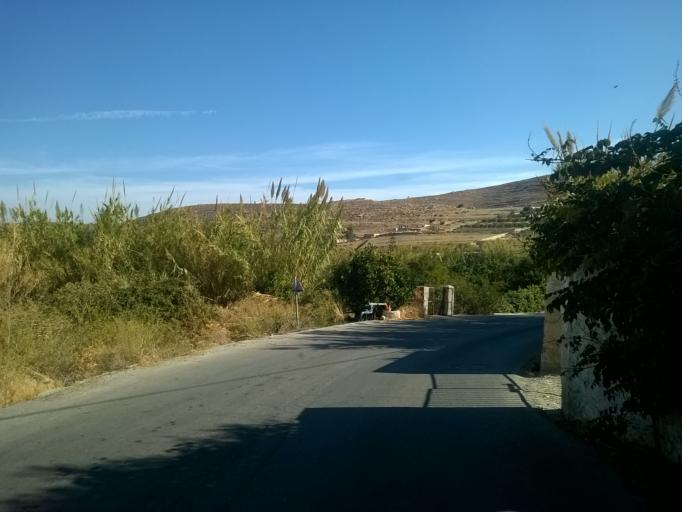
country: GR
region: South Aegean
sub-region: Nomos Kykladon
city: Naxos
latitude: 37.1180
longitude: 25.4364
